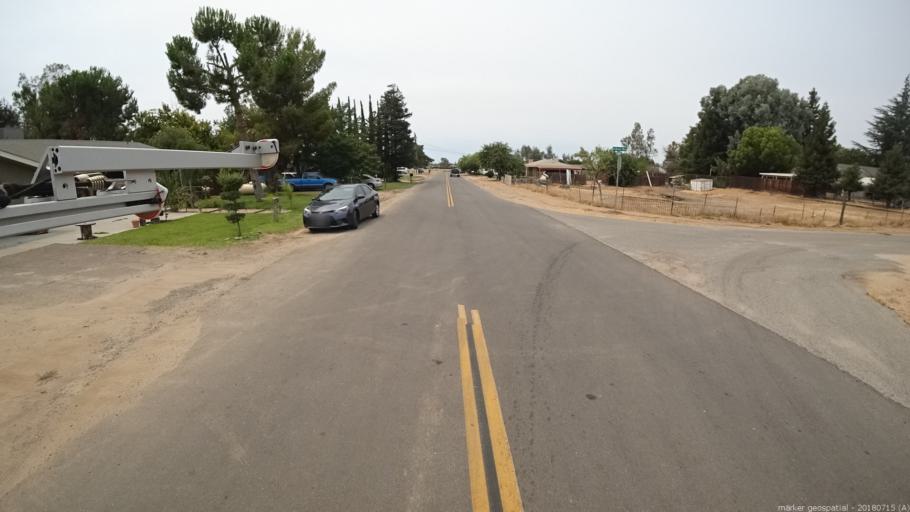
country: US
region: California
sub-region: Madera County
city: Madera Acres
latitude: 37.0232
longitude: -120.0791
